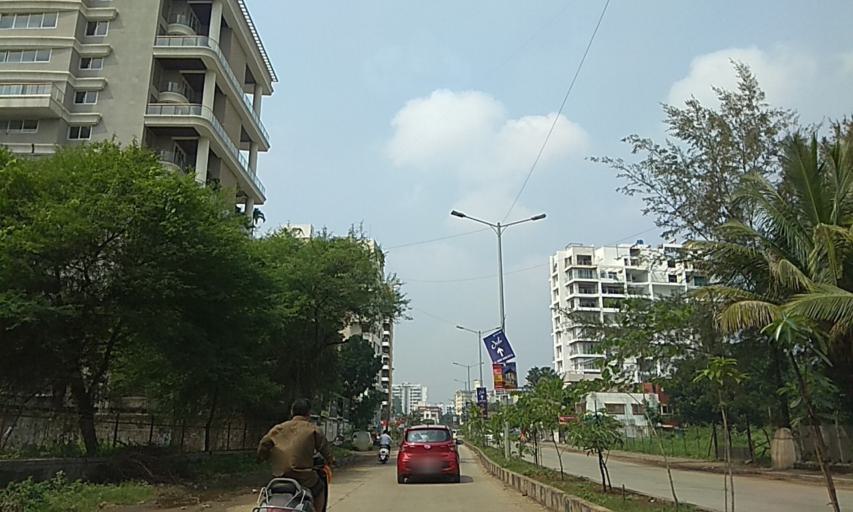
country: IN
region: Maharashtra
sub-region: Pune Division
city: Pimpri
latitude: 18.5594
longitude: 73.7823
